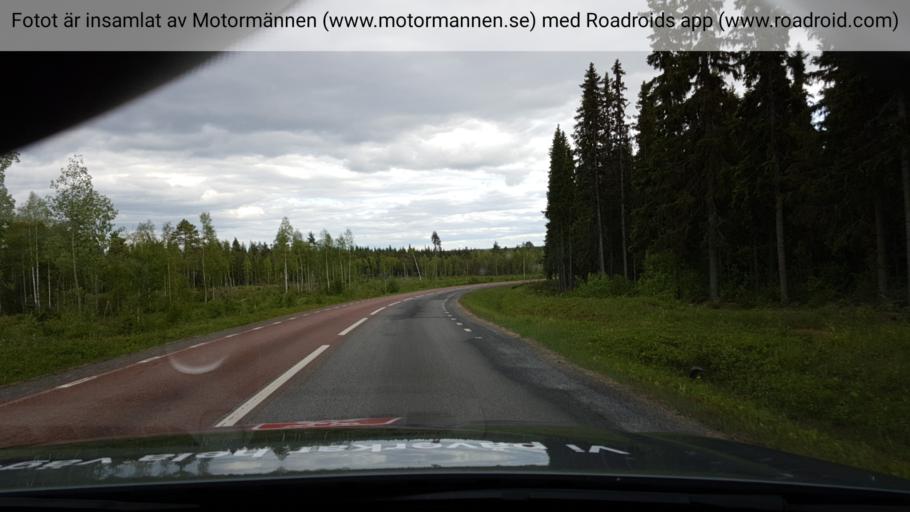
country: SE
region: Jaemtland
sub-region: Stroemsunds Kommun
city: Stroemsund
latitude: 63.8127
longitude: 15.5209
